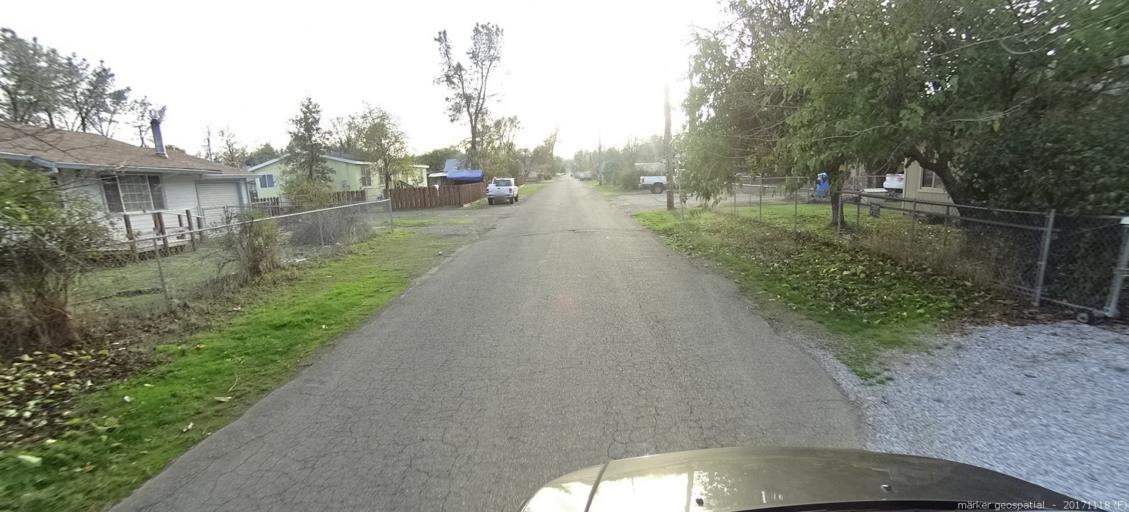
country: US
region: California
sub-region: Shasta County
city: Anderson
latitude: 40.4637
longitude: -122.3303
